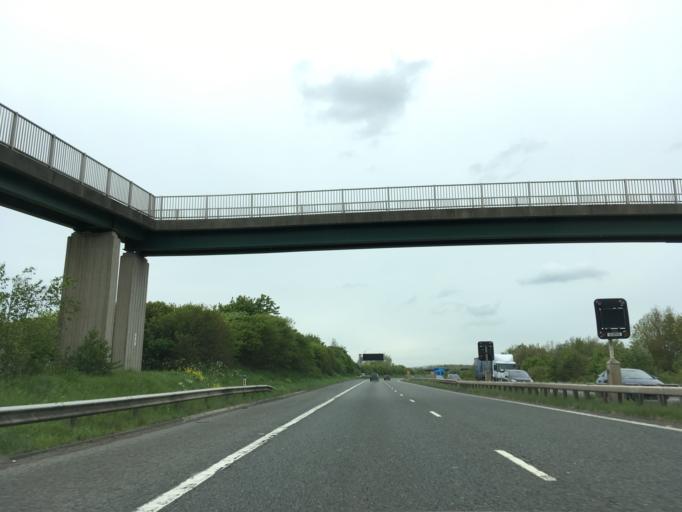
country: GB
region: England
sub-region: South Gloucestershire
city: Severn Beach
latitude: 51.5615
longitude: -2.6554
